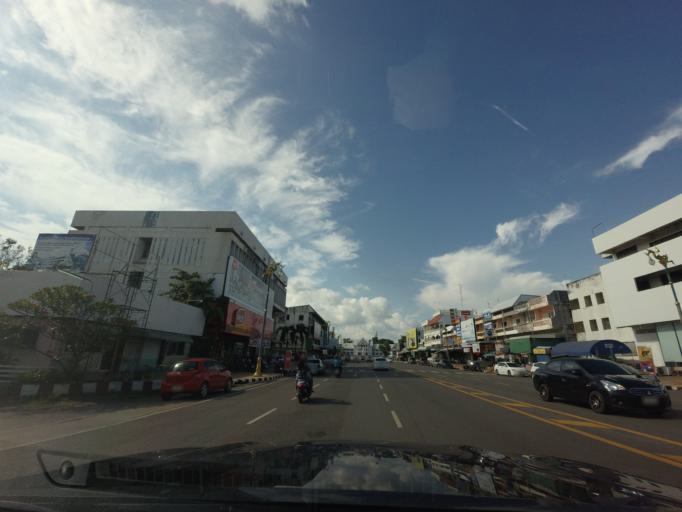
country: TH
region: Nong Khai
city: Nong Khai
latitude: 17.8773
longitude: 102.7416
